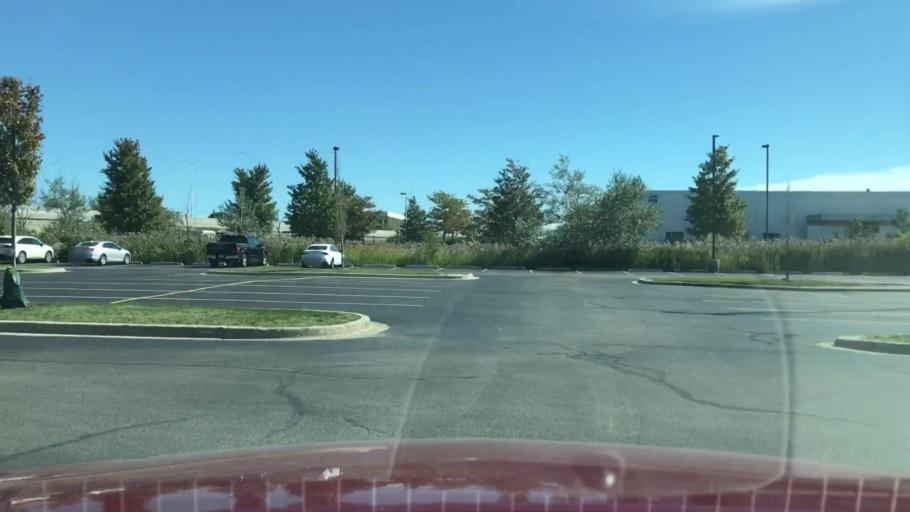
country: US
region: Illinois
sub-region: Cook County
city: Rosemont
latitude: 42.0078
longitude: -87.9050
